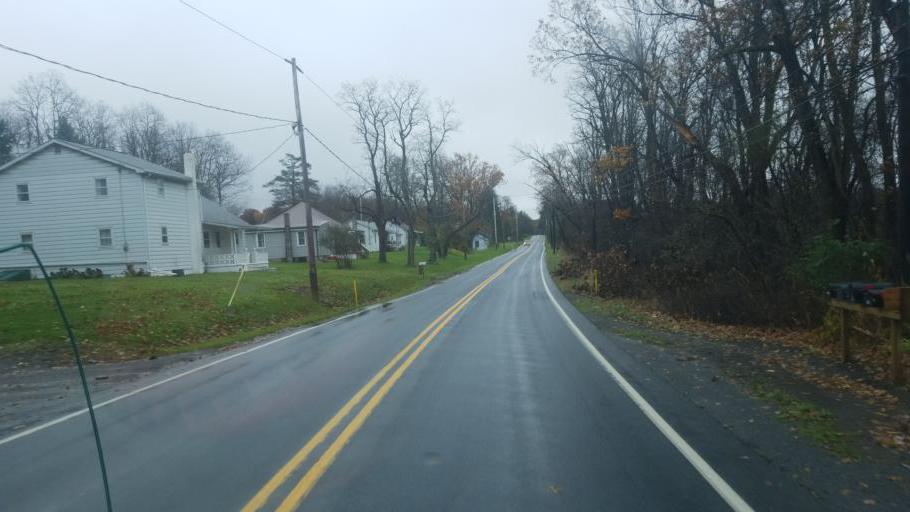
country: US
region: Pennsylvania
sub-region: Centre County
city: Milesburg
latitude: 41.0300
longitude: -77.9790
